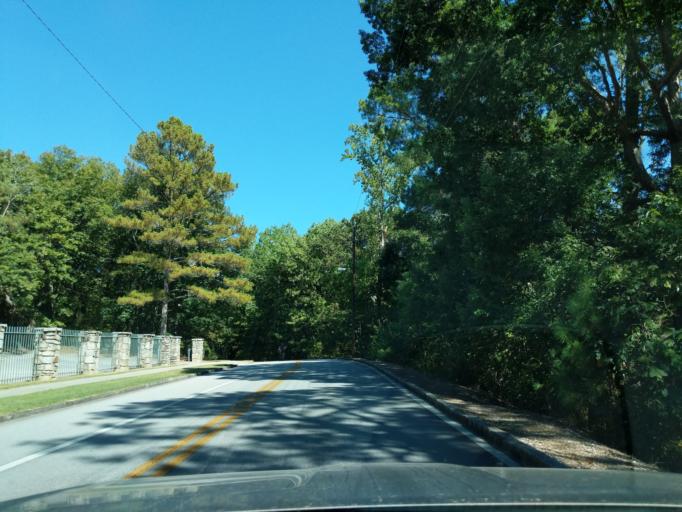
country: US
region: Georgia
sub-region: DeKalb County
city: Stone Mountain
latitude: 33.7984
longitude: -84.1394
